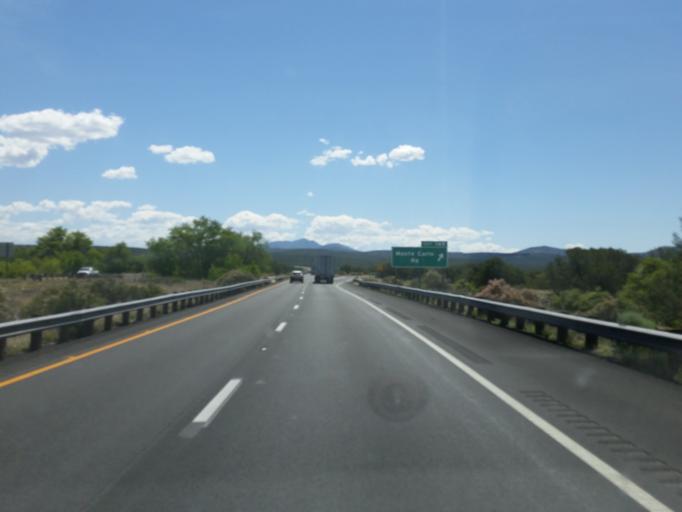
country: US
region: Arizona
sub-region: Coconino County
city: Williams
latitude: 35.2144
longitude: -112.4294
